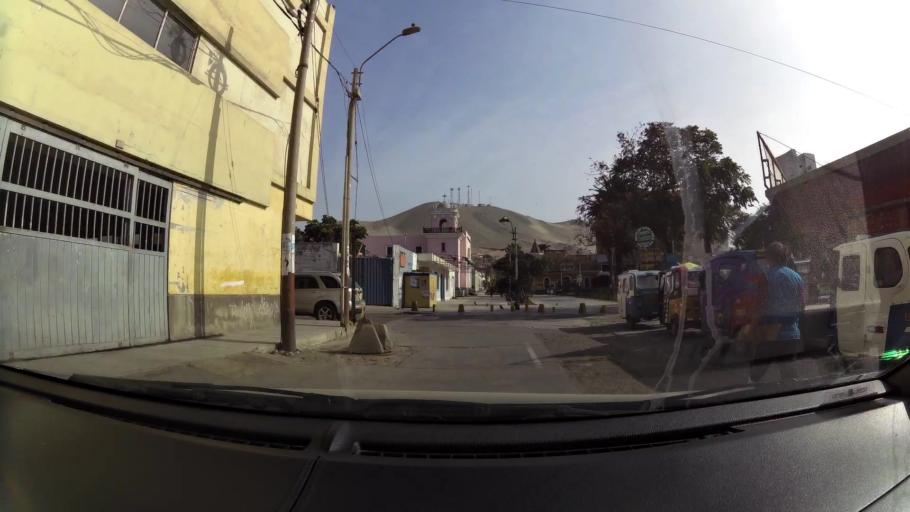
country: PE
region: Lima
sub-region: Lima
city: Santa Rosa
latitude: -11.7736
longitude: -77.1744
